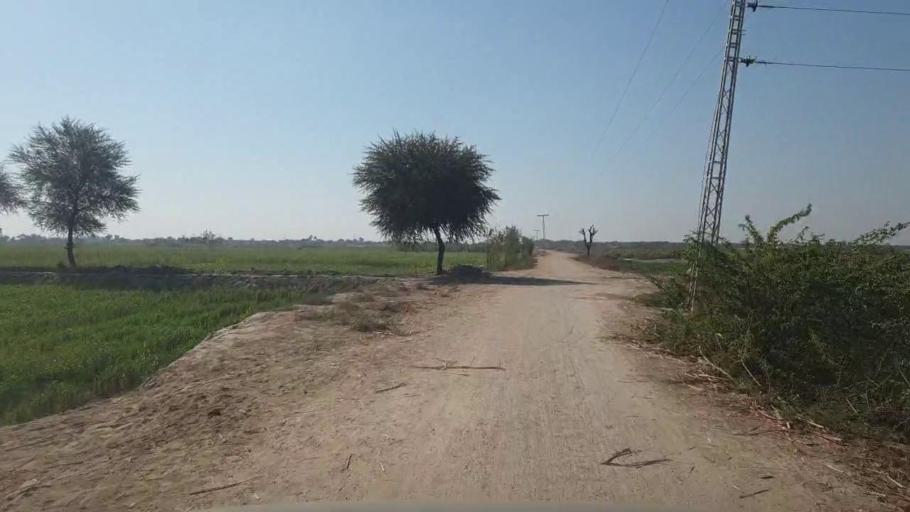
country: PK
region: Sindh
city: Mirwah Gorchani
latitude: 25.2690
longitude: 69.1086
